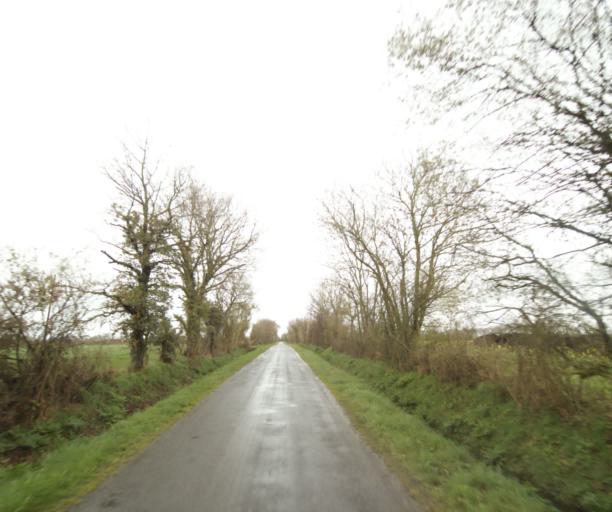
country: FR
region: Pays de la Loire
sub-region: Departement de la Loire-Atlantique
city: Bouvron
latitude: 47.4493
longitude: -1.8783
